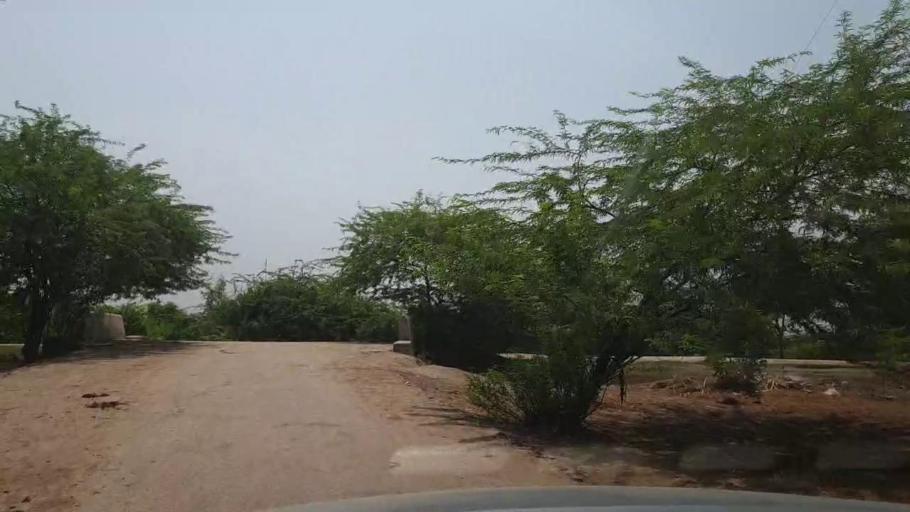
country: PK
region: Sindh
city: Garhi Yasin
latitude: 27.8769
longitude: 68.4953
